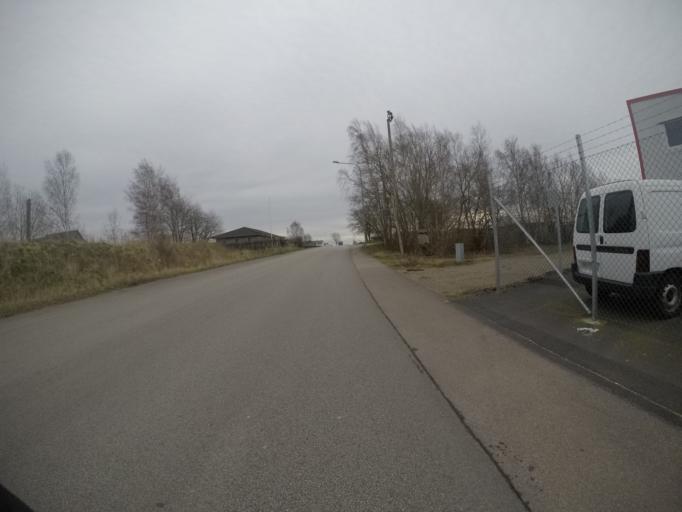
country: SE
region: Halland
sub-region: Laholms Kommun
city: Laholm
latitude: 56.5101
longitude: 13.0556
